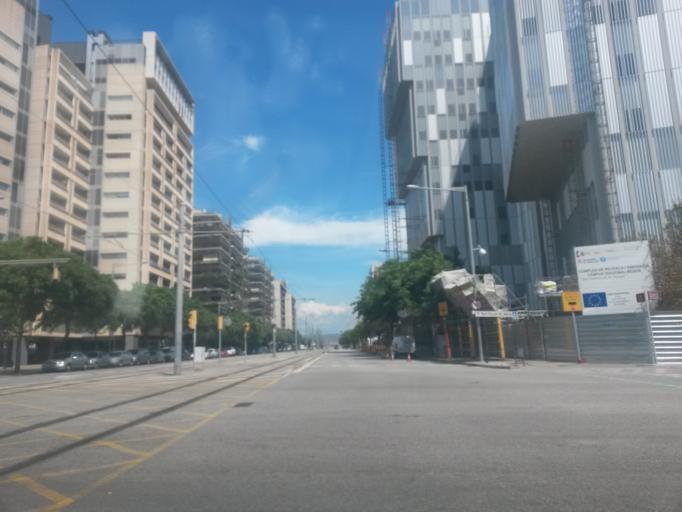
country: ES
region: Catalonia
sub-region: Provincia de Barcelona
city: Sant Adria de Besos
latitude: 41.4134
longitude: 2.2213
